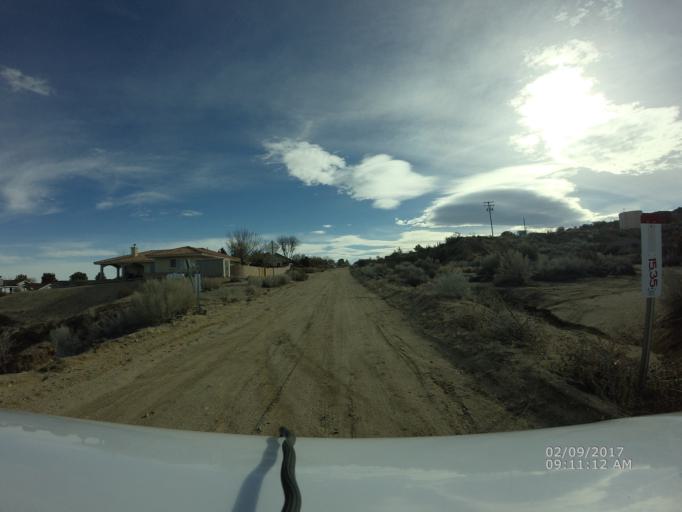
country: US
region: California
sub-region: Los Angeles County
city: Littlerock
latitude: 34.4684
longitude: -117.8528
